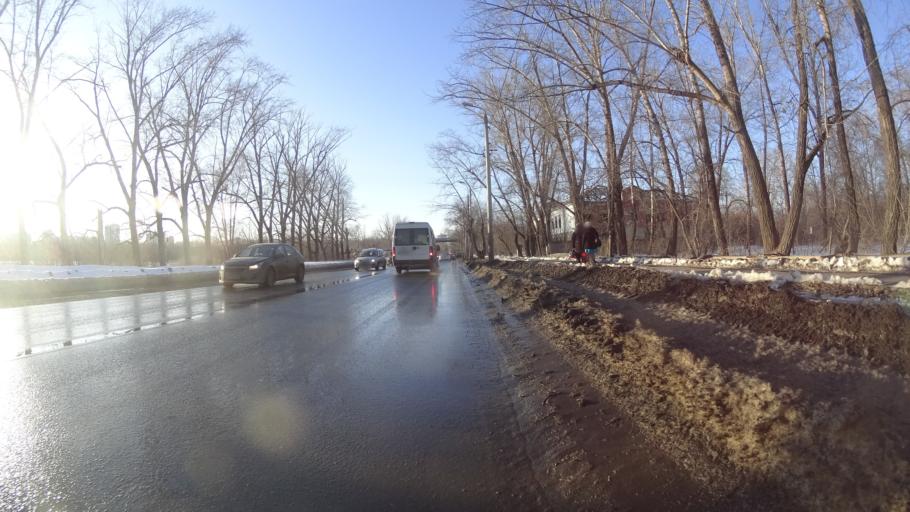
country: RU
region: Chelyabinsk
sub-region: Gorod Chelyabinsk
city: Chelyabinsk
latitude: 55.1313
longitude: 61.4635
